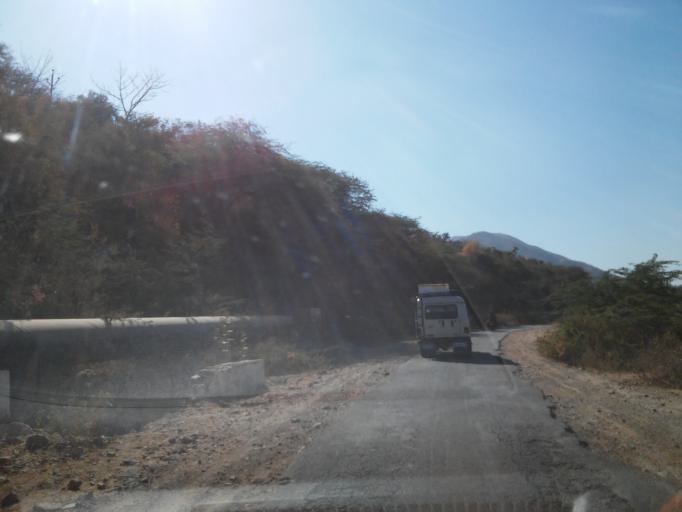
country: IN
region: Rajasthan
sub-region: Udaipur
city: Udaipur
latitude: 24.5318
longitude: 73.6240
